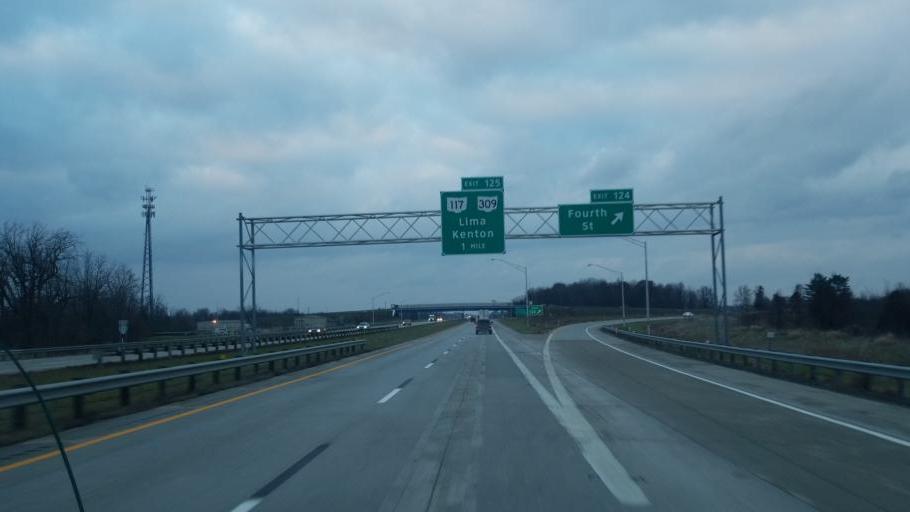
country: US
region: Ohio
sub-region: Allen County
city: Lima
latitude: 40.7133
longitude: -84.0751
